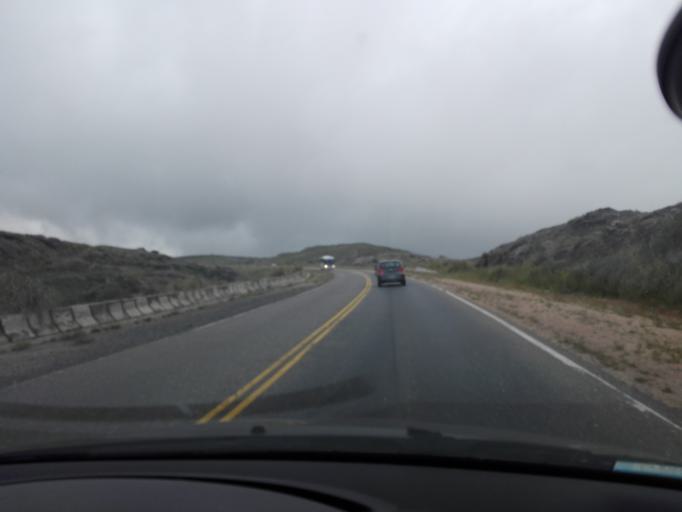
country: AR
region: Cordoba
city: Cuesta Blanca
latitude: -31.6130
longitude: -64.7473
